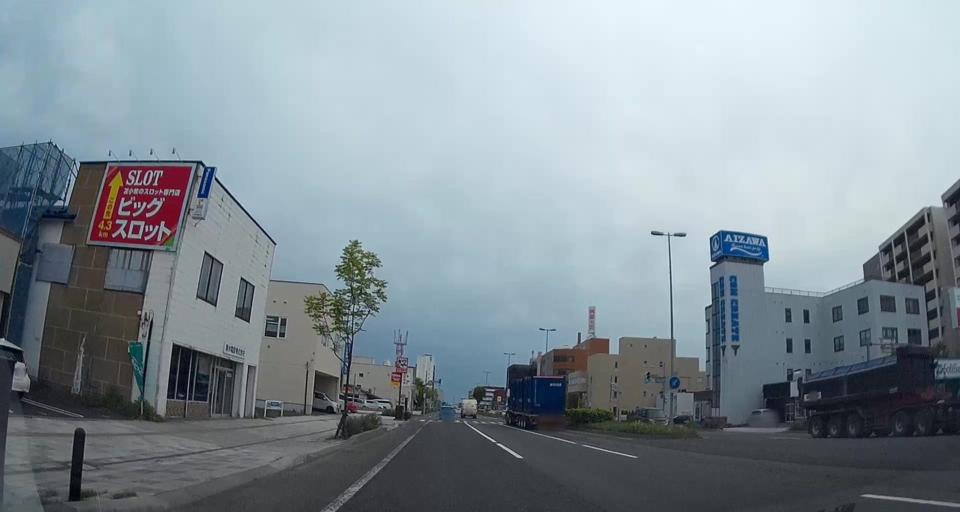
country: JP
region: Hokkaido
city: Tomakomai
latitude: 42.6360
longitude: 141.6069
